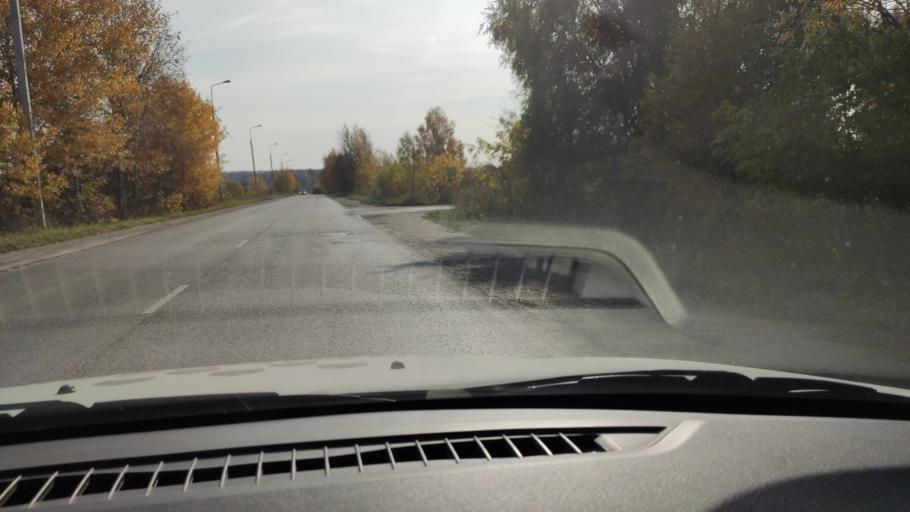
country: RU
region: Perm
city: Novyye Lyady
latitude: 58.0455
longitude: 56.5924
